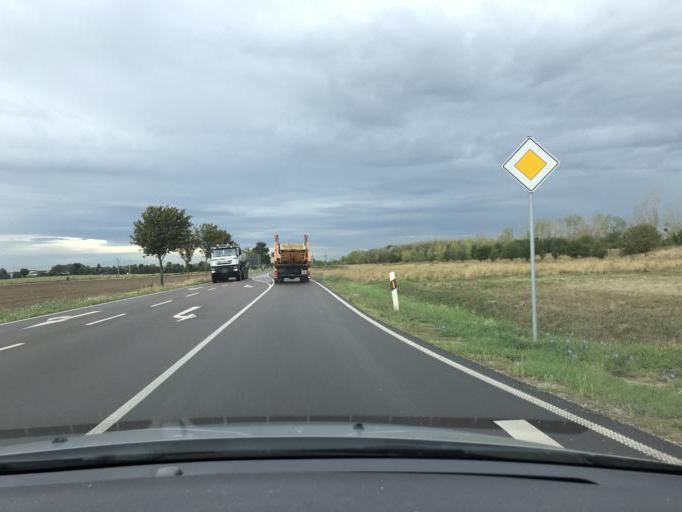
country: DE
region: Saxony-Anhalt
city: Gross Rosenburg
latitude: 51.8789
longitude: 11.8590
